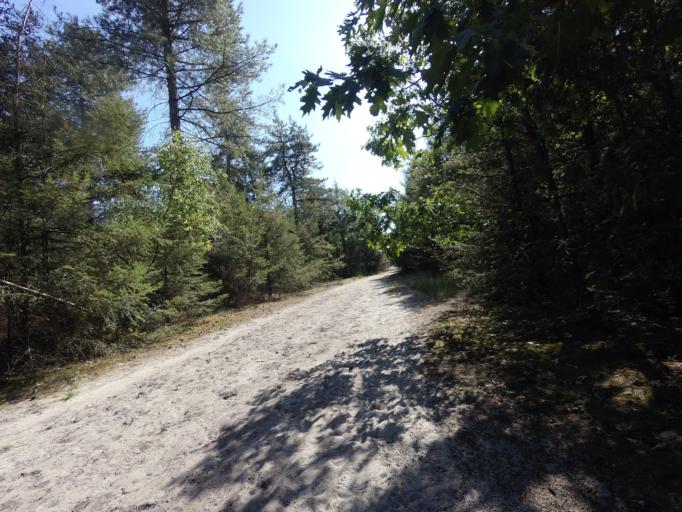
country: NL
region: North Brabant
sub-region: Gemeente Someren
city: Someren
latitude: 51.3663
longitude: 5.6636
